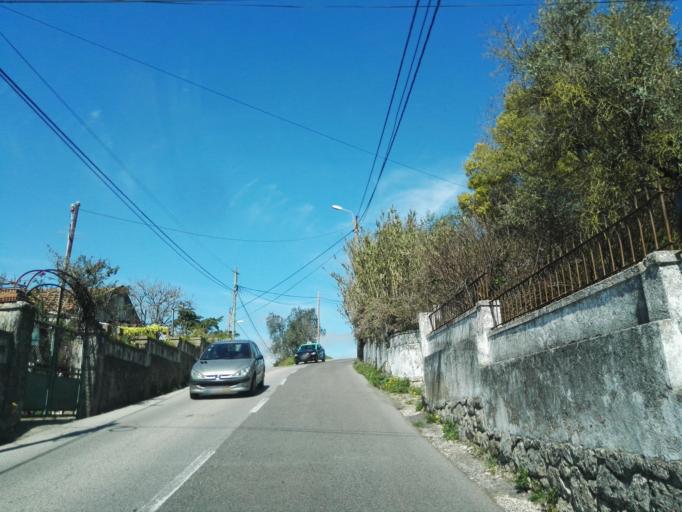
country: PT
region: Lisbon
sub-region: Sintra
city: Rio de Mouro
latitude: 38.7607
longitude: -9.3295
